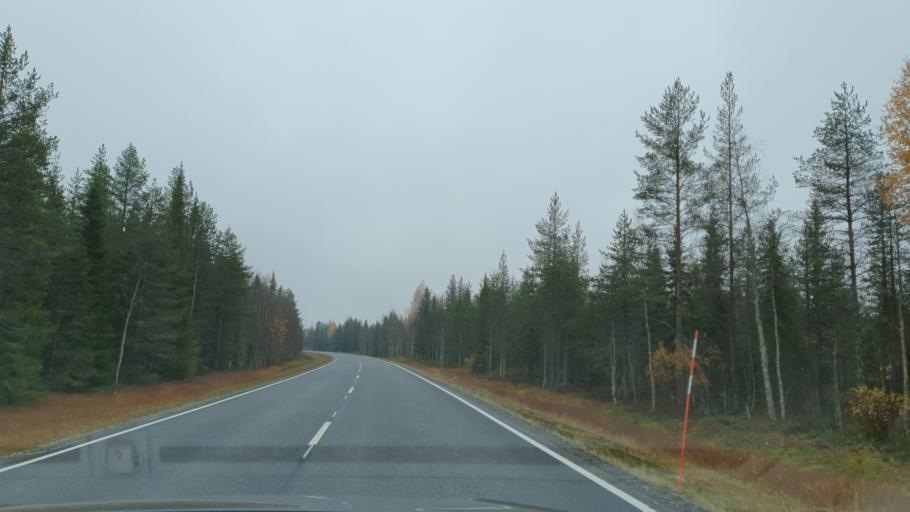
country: FI
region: Lapland
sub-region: Rovaniemi
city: Ranua
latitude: 66.1331
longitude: 26.2793
